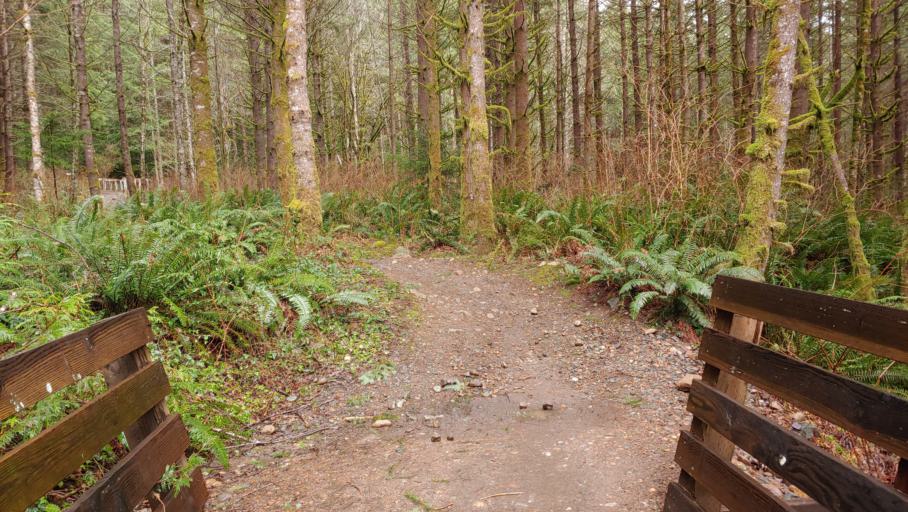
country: US
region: Washington
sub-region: King County
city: Hobart
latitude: 47.4686
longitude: -121.9360
